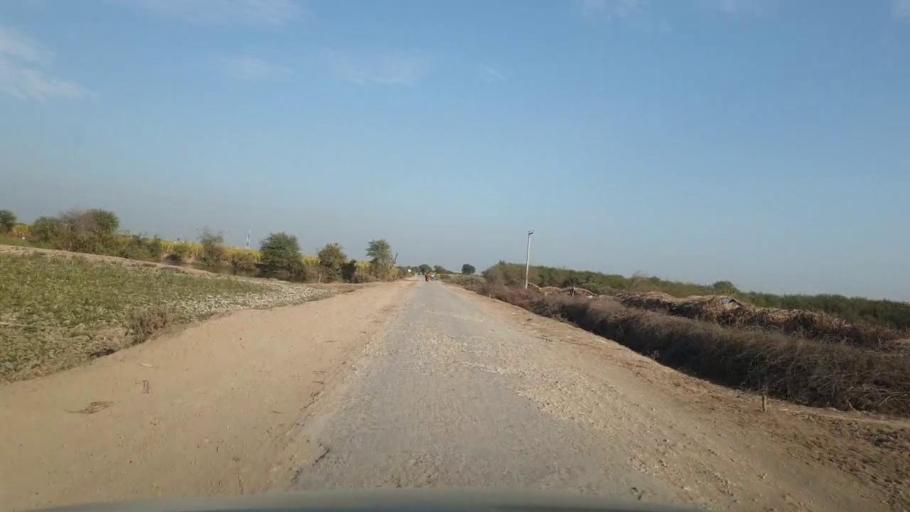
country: PK
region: Sindh
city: Tando Allahyar
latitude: 25.5936
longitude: 68.6795
